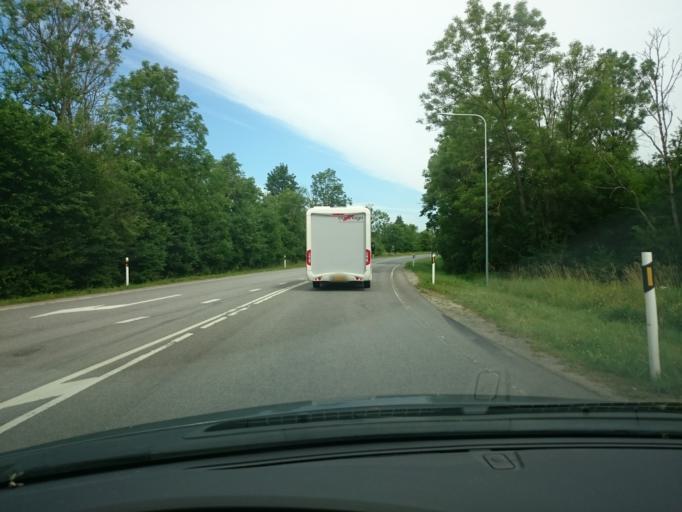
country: EE
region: Laeaene
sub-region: Ridala Parish
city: Uuemoisa
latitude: 58.9582
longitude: 23.6684
